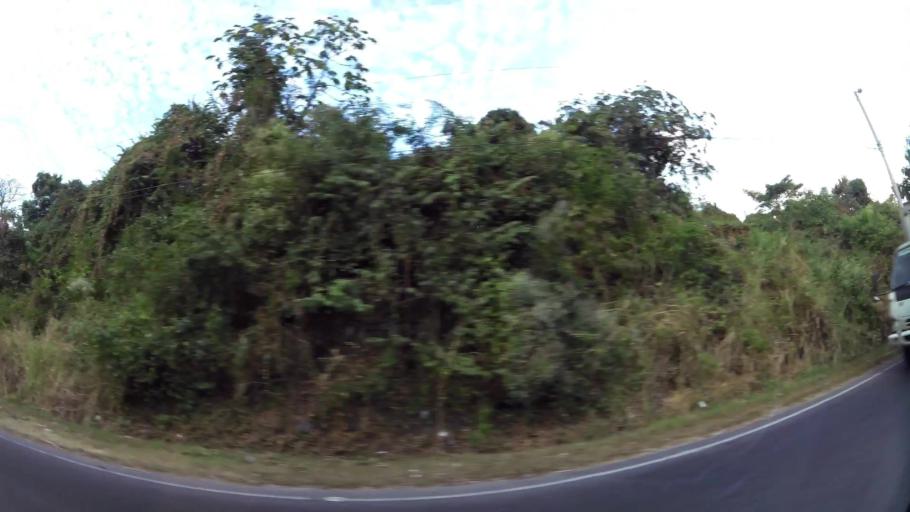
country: SV
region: San Vicente
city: Apastepeque
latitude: 13.6660
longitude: -88.7945
